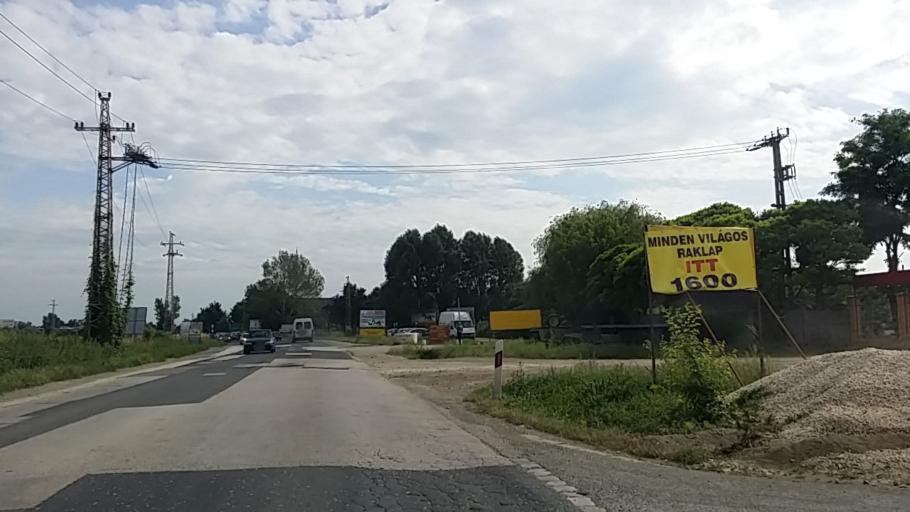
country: HU
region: Pest
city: Szigetszentmiklos
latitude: 47.3843
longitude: 19.0497
